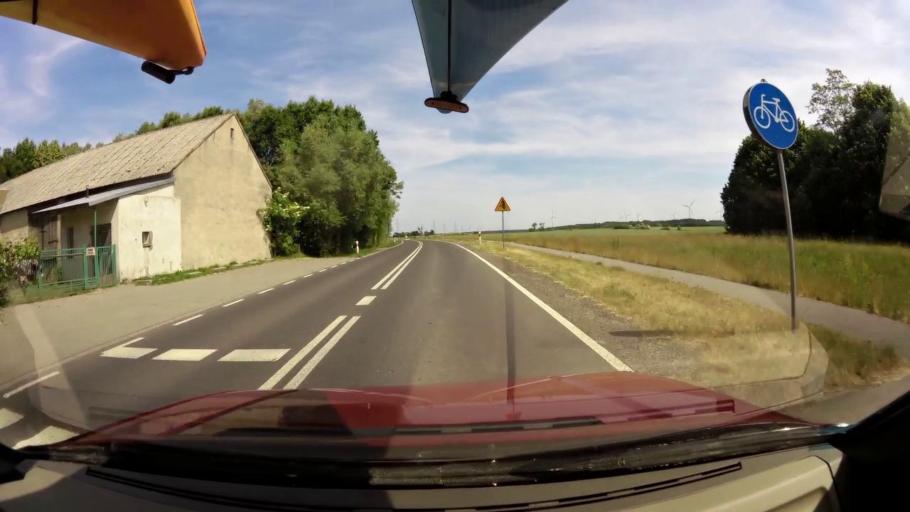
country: PL
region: West Pomeranian Voivodeship
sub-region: Powiat koszalinski
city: Sianow
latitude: 54.2970
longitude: 16.3062
